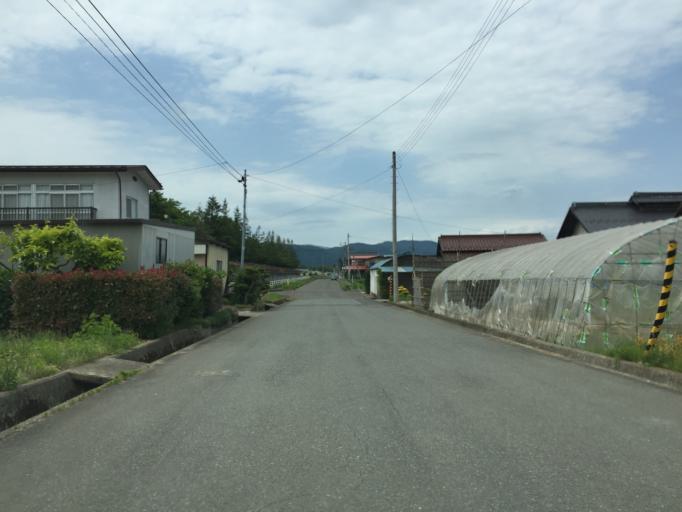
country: JP
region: Fukushima
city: Fukushima-shi
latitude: 37.7369
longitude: 140.4029
